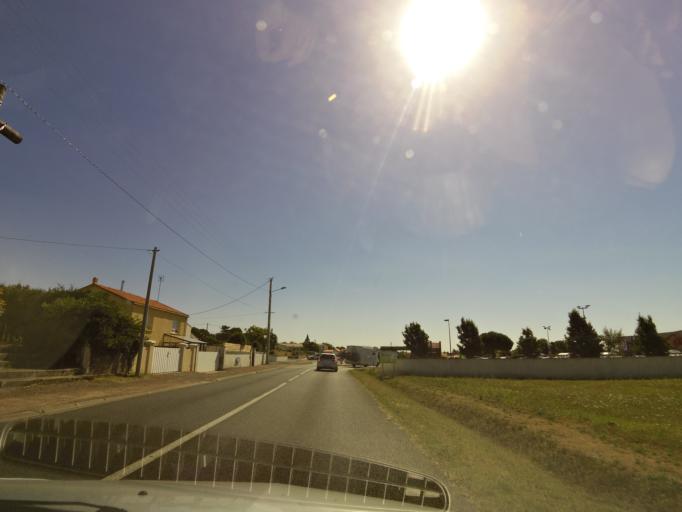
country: FR
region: Pays de la Loire
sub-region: Departement de la Vendee
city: Longeville-sur-Mer
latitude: 46.4252
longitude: -1.4966
